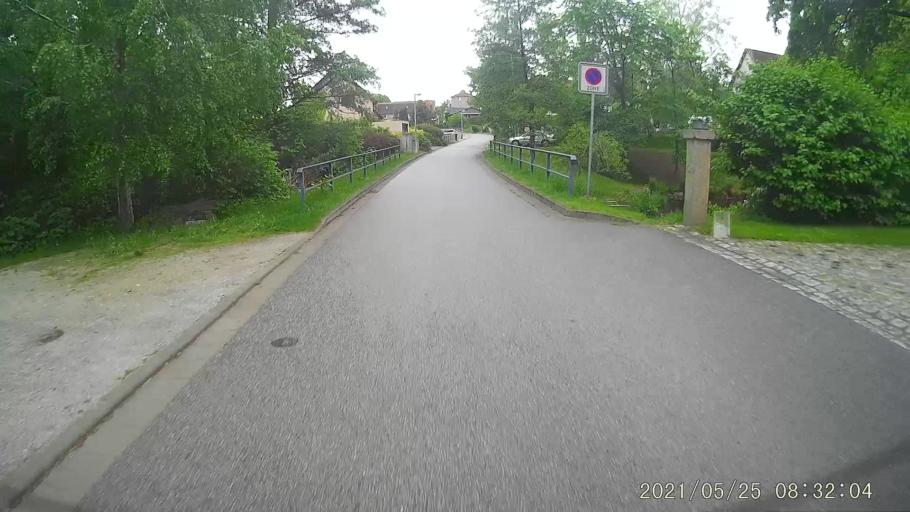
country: DE
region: Saxony
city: Bautzen
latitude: 51.1812
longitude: 14.4614
